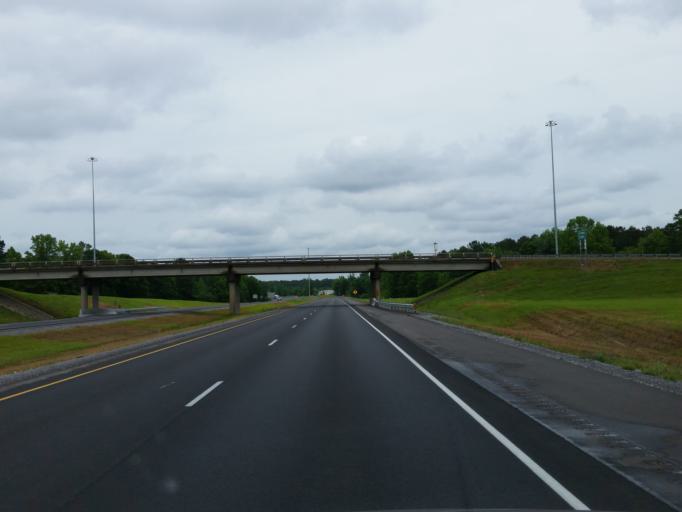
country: US
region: Mississippi
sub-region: Jones County
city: Sharon
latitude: 31.9067
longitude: -89.0160
